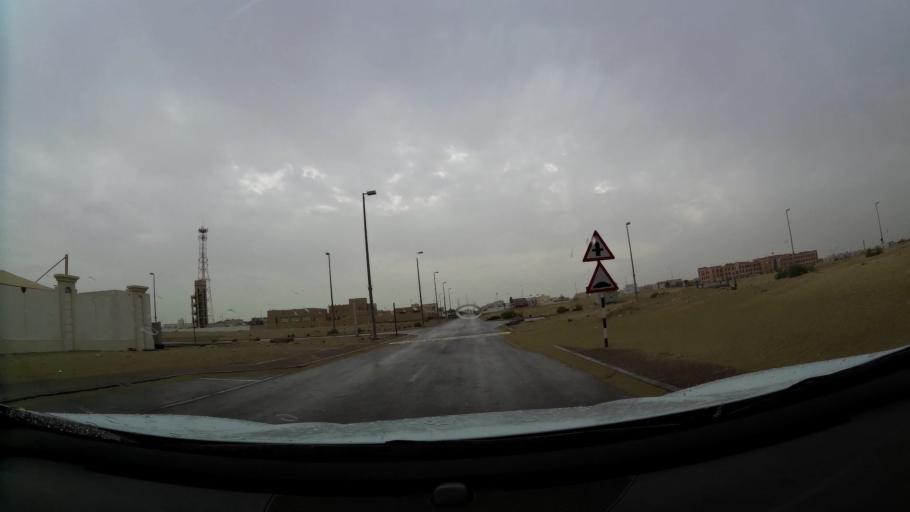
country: AE
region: Abu Dhabi
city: Abu Dhabi
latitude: 24.3622
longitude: 54.6381
